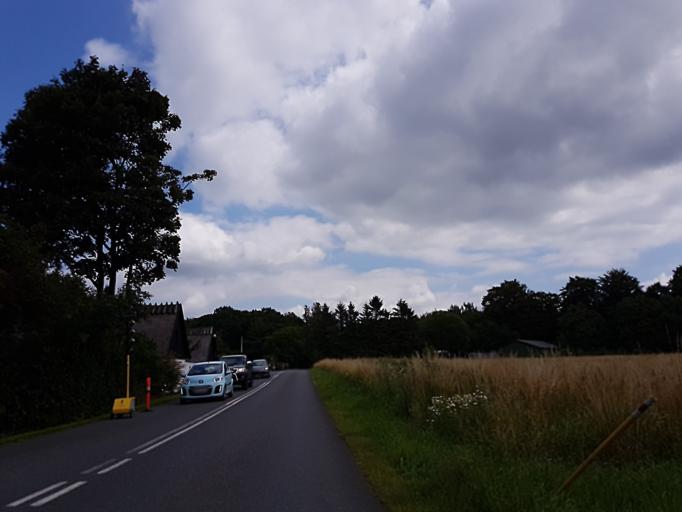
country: DK
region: Capital Region
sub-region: Allerod Kommune
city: Lynge
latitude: 55.8109
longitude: 12.2964
